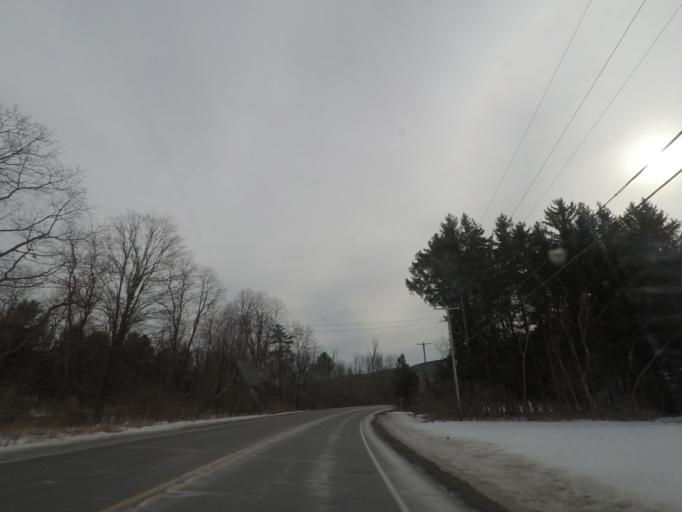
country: US
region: New York
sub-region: Albany County
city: Voorheesville
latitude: 42.5887
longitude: -73.9832
